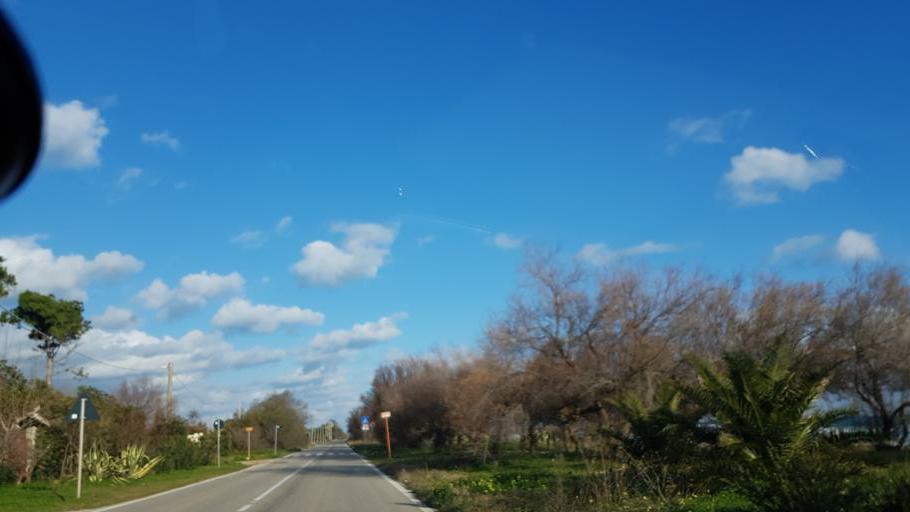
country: IT
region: Apulia
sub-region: Provincia di Brindisi
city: Materdomini
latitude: 40.6712
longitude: 17.9461
